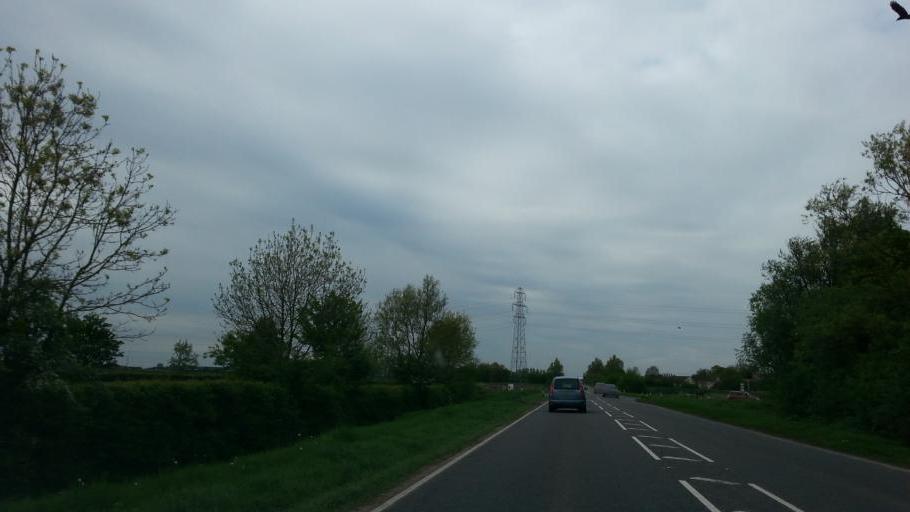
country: GB
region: England
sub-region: Cambridgeshire
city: March
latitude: 52.5490
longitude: 0.0697
